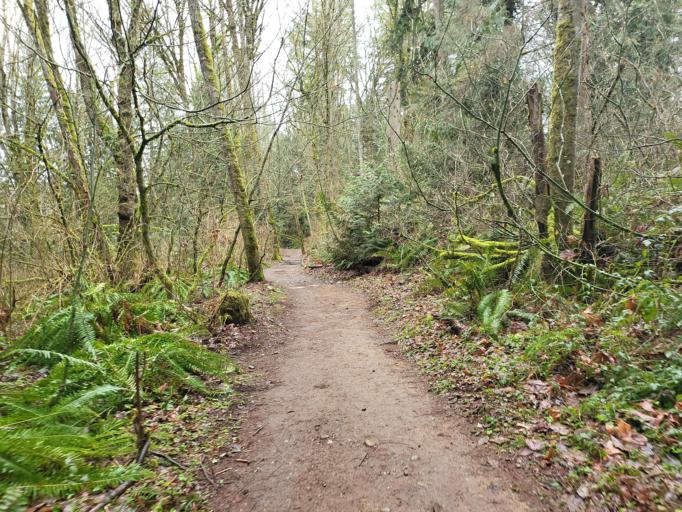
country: US
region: Washington
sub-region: King County
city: Newcastle
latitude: 47.5304
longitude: -122.1281
